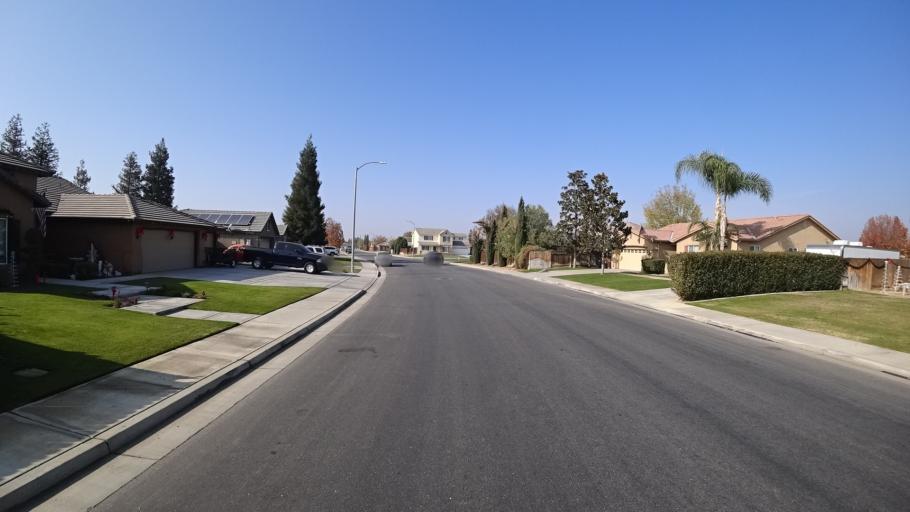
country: US
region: California
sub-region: Kern County
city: Greenacres
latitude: 35.4181
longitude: -119.1235
